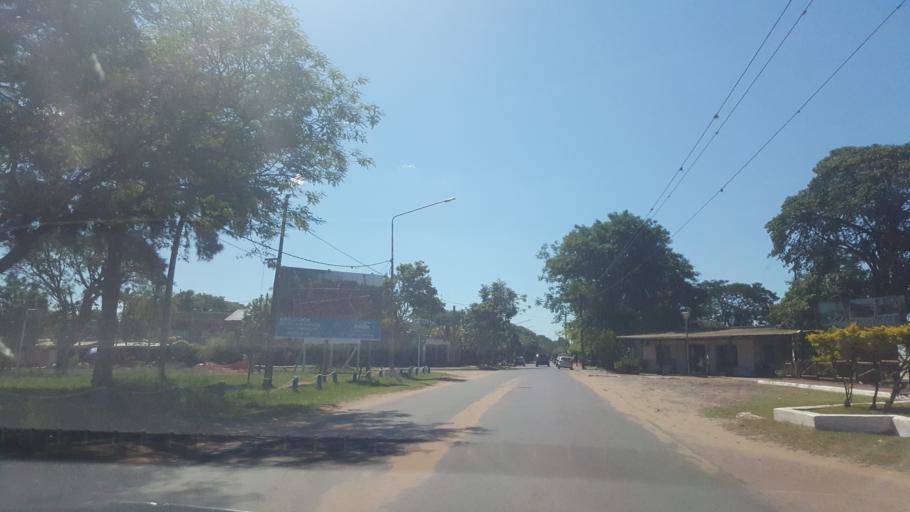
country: AR
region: Corrientes
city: Ituzaingo
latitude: -27.5915
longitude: -56.6866
